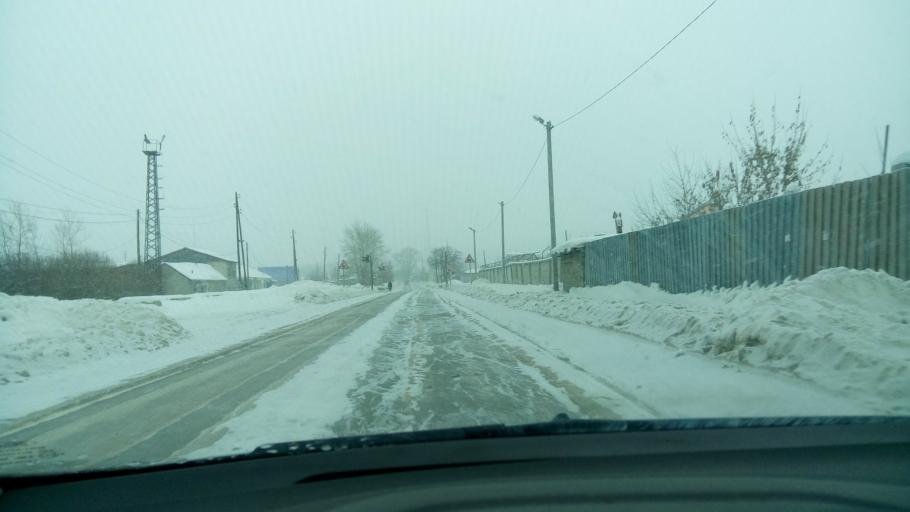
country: RU
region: Sverdlovsk
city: Bogdanovich
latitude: 56.7804
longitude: 62.0278
